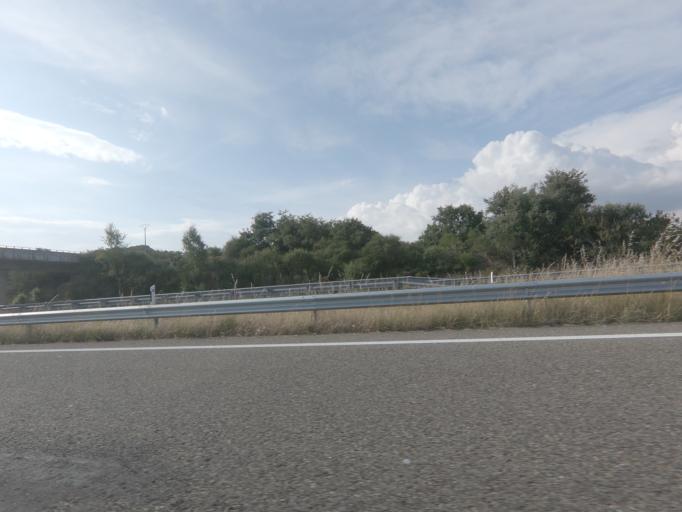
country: ES
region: Galicia
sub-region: Provincia de Ourense
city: Xinzo de Limia
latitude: 42.0642
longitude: -7.6884
